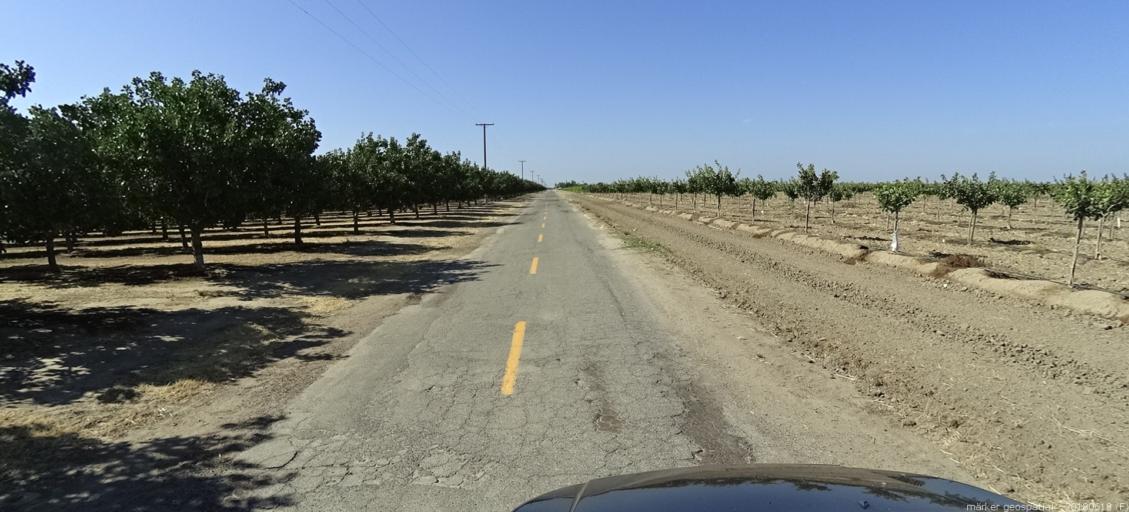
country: US
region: California
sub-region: Madera County
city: Parkwood
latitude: 36.8926
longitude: -120.1558
